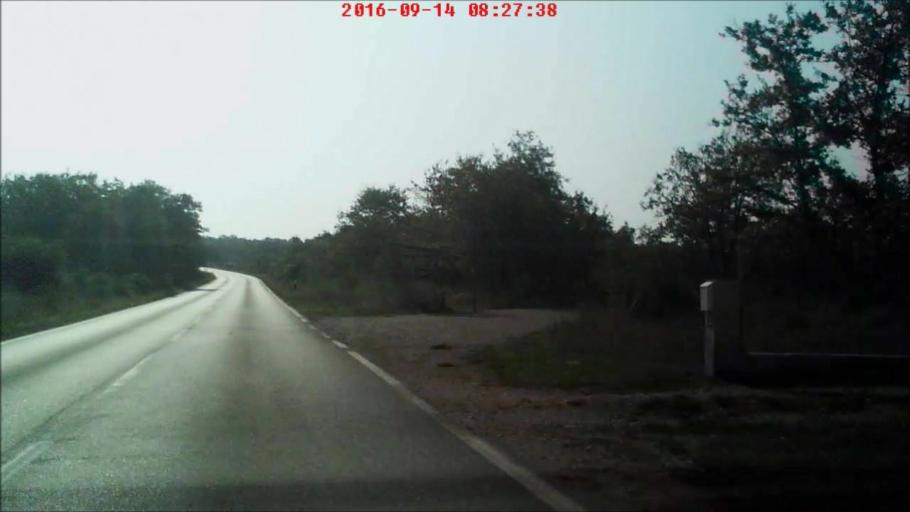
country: HR
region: Zadarska
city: Zadar
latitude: 44.1877
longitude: 15.2681
